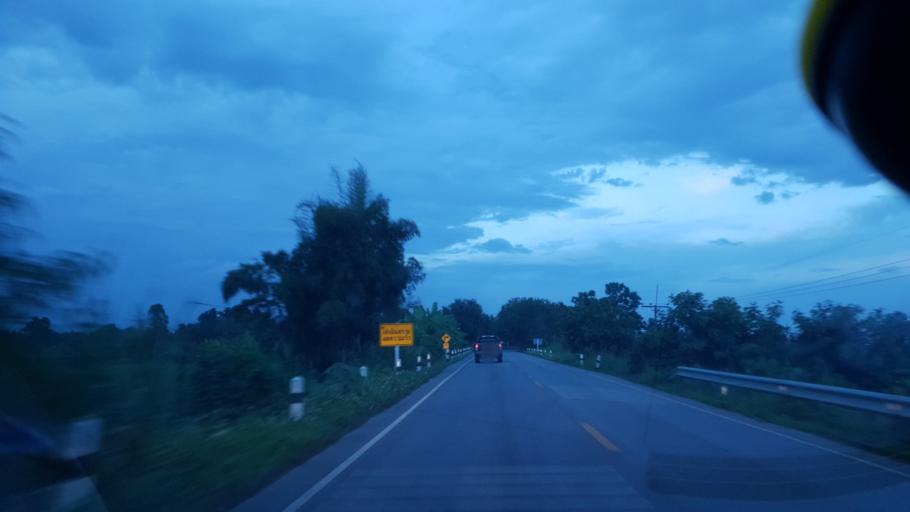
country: TH
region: Chiang Rai
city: Wiang Chiang Rung
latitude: 19.9728
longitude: 99.9739
